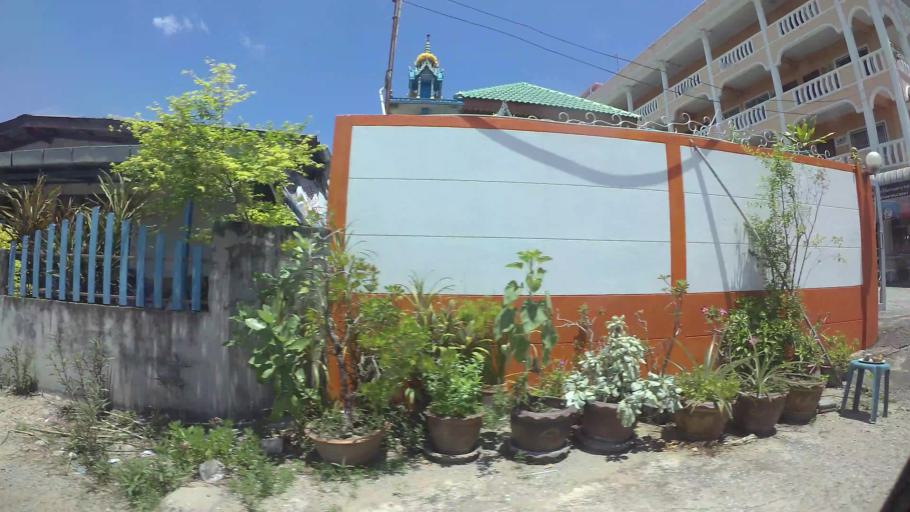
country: TH
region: Chon Buri
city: Si Racha
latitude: 13.1123
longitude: 100.9347
